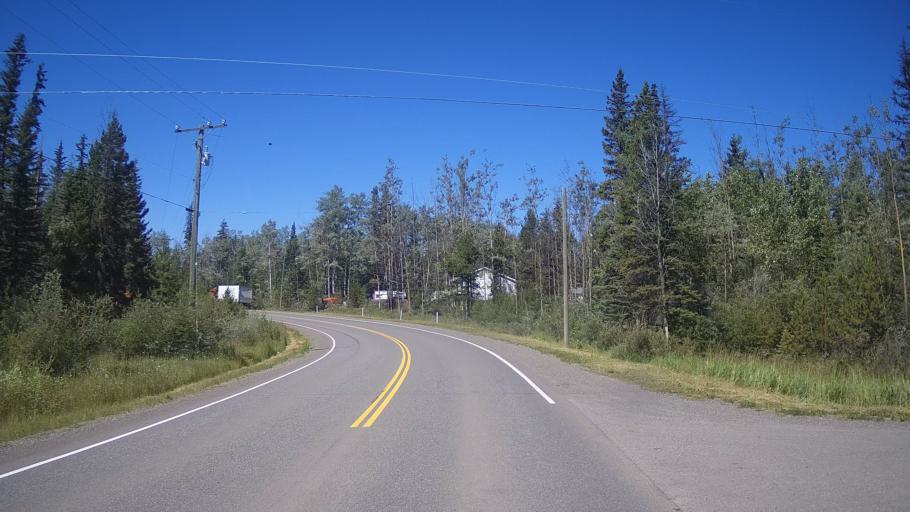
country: CA
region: British Columbia
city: Cache Creek
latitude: 51.5549
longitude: -121.2187
